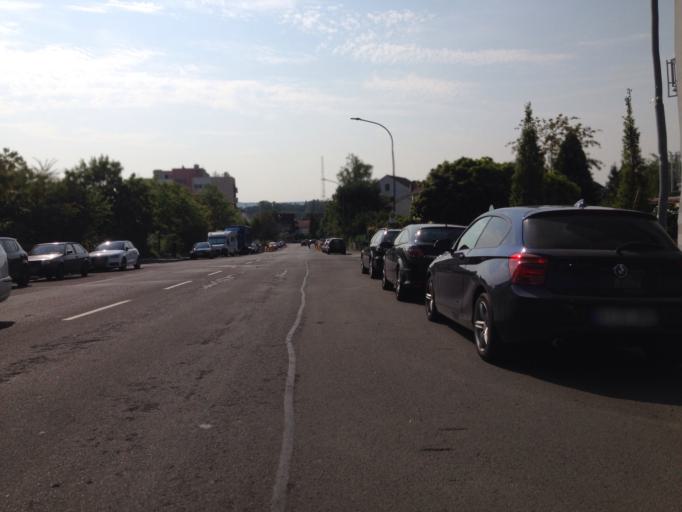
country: DE
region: Hesse
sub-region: Regierungsbezirk Giessen
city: Giessen
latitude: 50.6016
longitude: 8.6949
